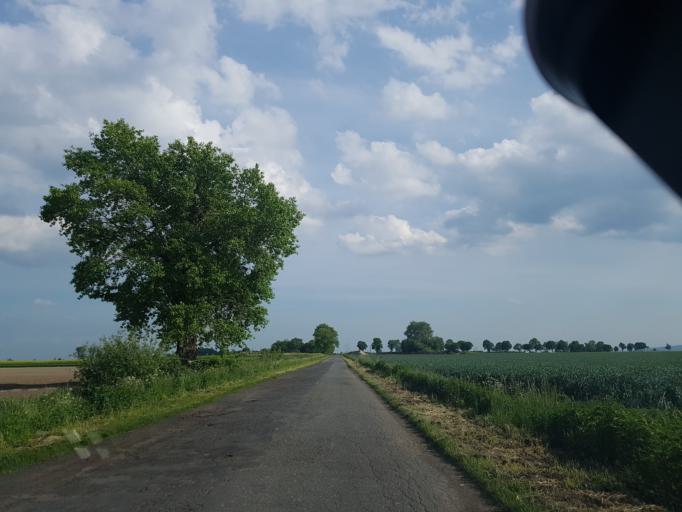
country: PL
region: Lower Silesian Voivodeship
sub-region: Powiat strzelinski
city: Wiazow
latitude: 50.8641
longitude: 17.1757
